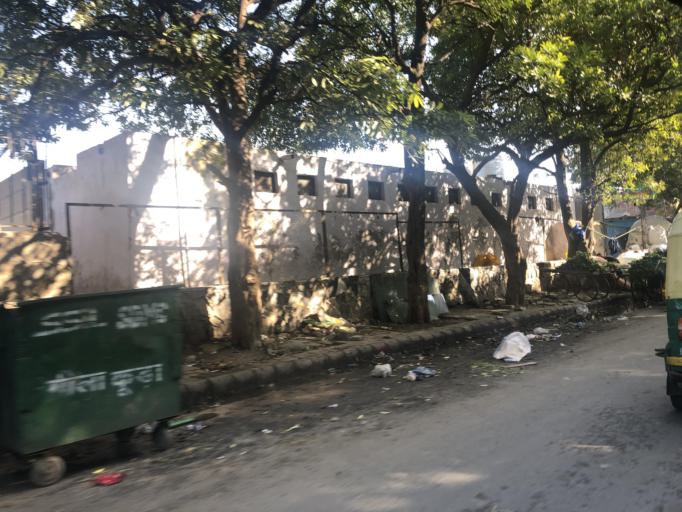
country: IN
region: NCT
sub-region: Central Delhi
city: Karol Bagh
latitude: 28.5540
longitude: 77.1651
